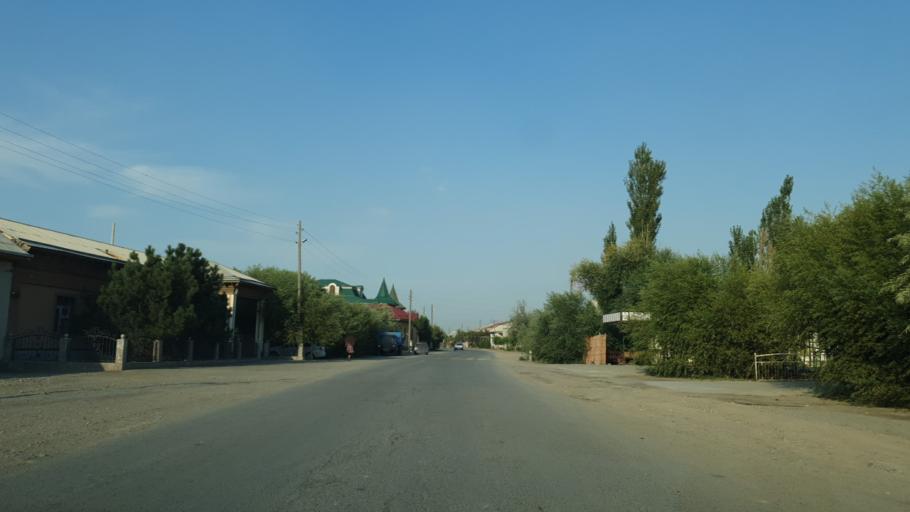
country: UZ
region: Fergana
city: Yaypan
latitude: 40.3705
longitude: 70.7712
